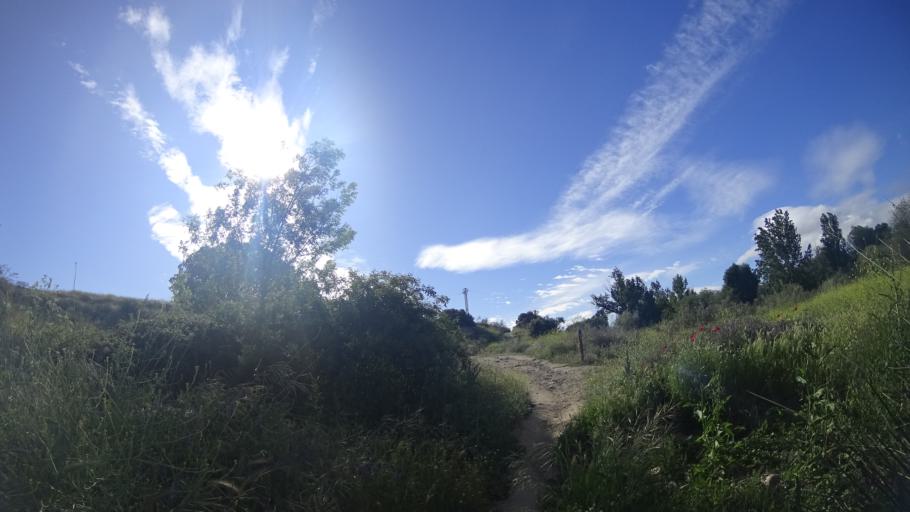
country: ES
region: Madrid
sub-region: Provincia de Madrid
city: Villanueva del Pardillo
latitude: 40.5133
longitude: -3.9388
